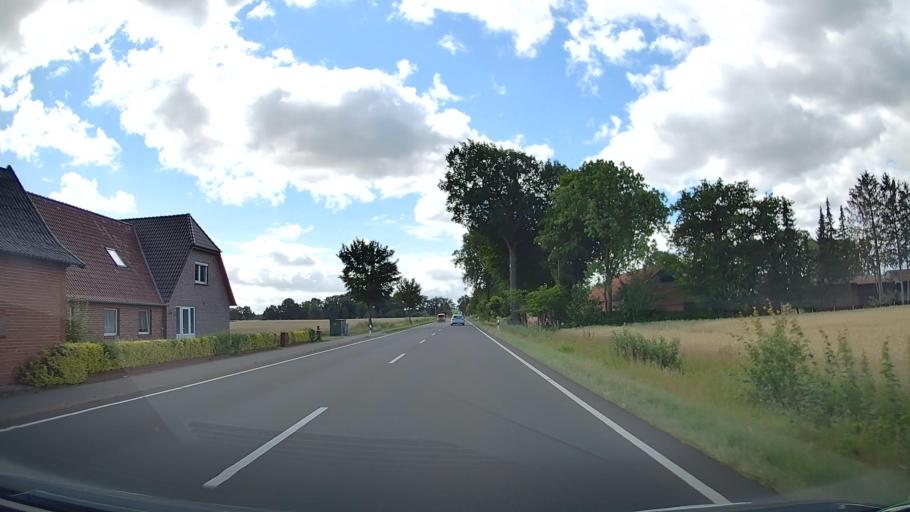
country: DE
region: Lower Saxony
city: Vechta
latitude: 52.6738
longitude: 8.3248
